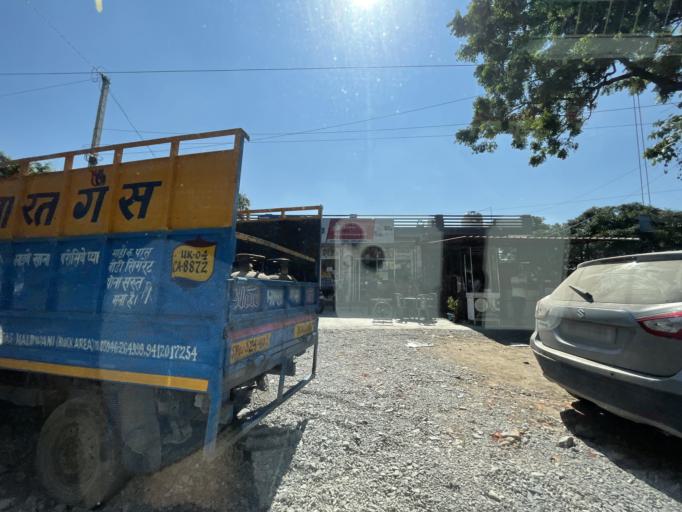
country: IN
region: Uttarakhand
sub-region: Naini Tal
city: Haldwani
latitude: 29.2147
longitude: 79.4800
